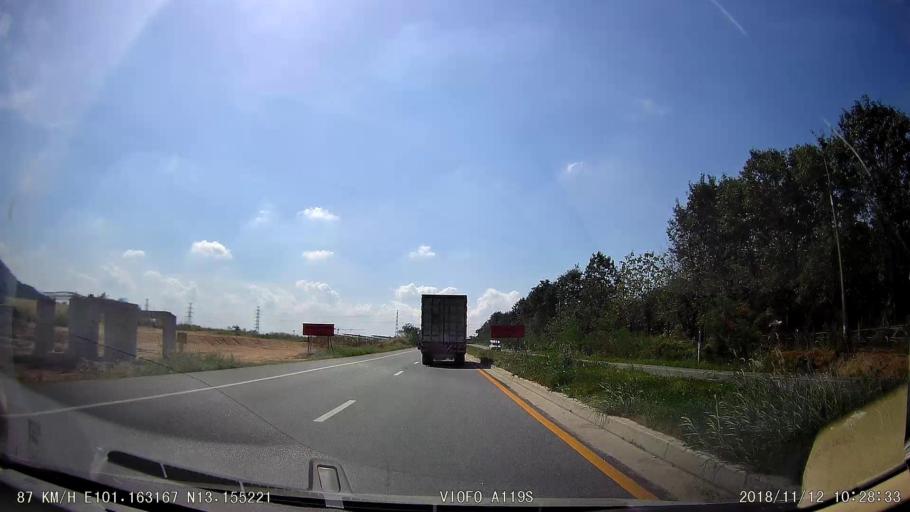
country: TH
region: Chon Buri
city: Ban Bueng
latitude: 13.1429
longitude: 101.1641
